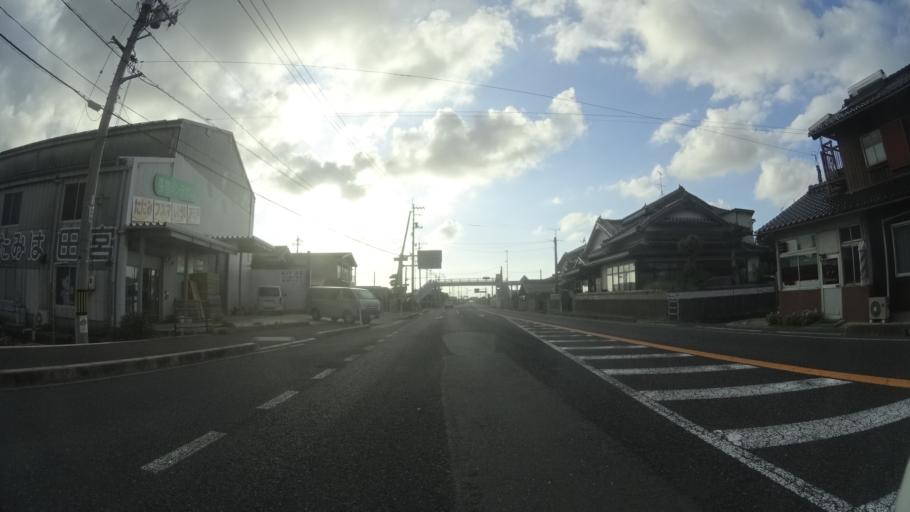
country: JP
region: Tottori
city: Kurayoshi
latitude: 35.5240
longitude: 133.5888
